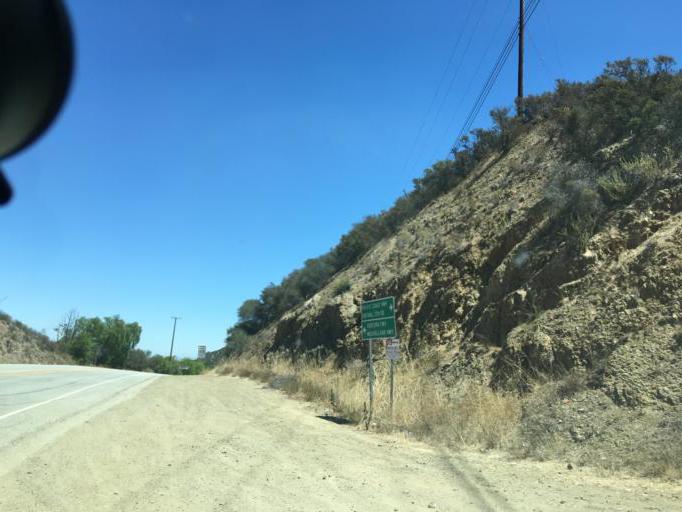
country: US
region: California
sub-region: Los Angeles County
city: Westlake Village
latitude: 34.0941
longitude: -118.8285
